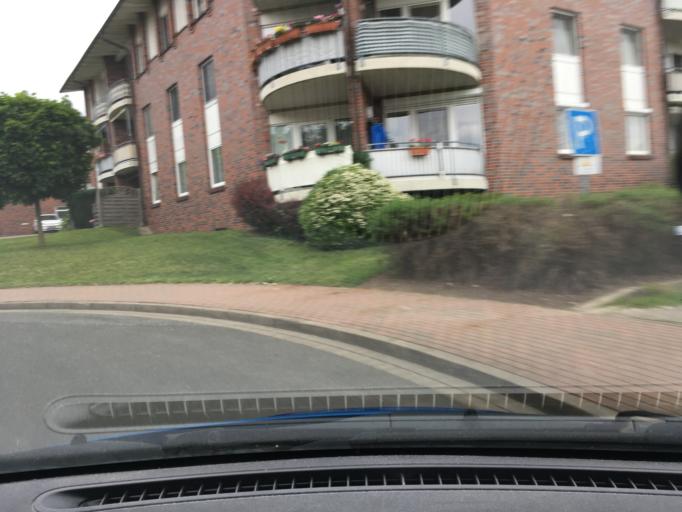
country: DE
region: Lower Saxony
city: Lueneburg
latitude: 53.2515
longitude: 10.3867
